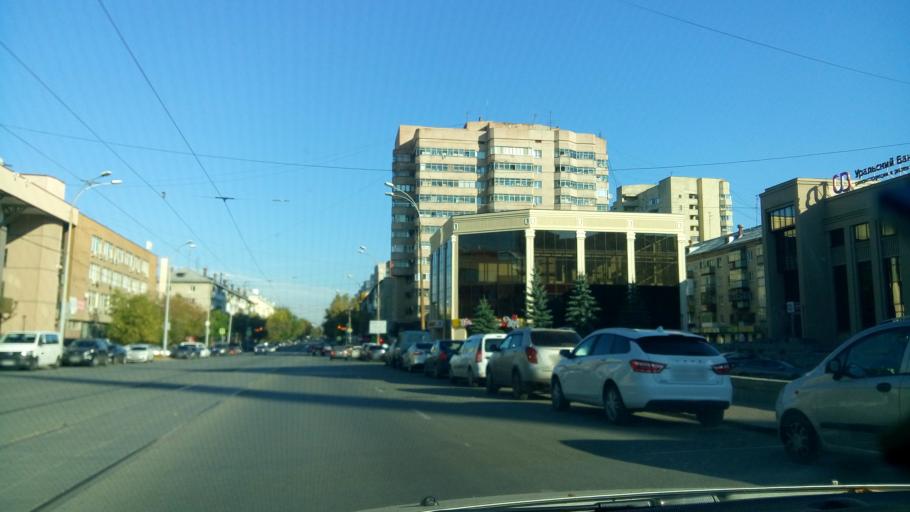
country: RU
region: Sverdlovsk
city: Yekaterinburg
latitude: 56.8439
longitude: 60.6191
